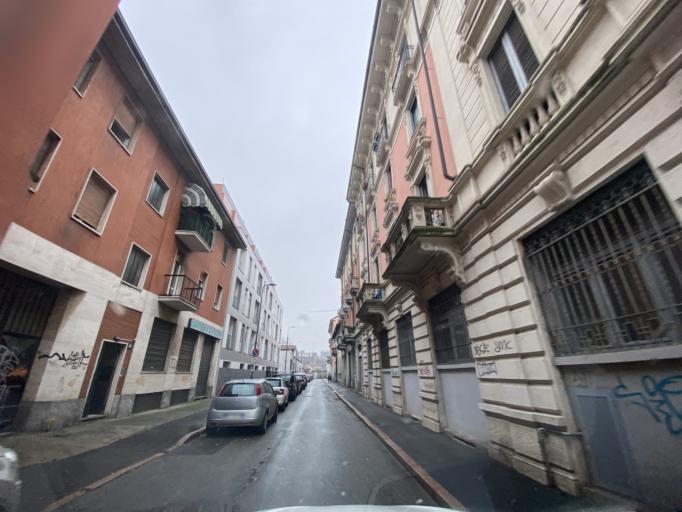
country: IT
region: Lombardy
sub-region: Citta metropolitana di Milano
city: Milano
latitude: 45.5008
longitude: 9.1748
